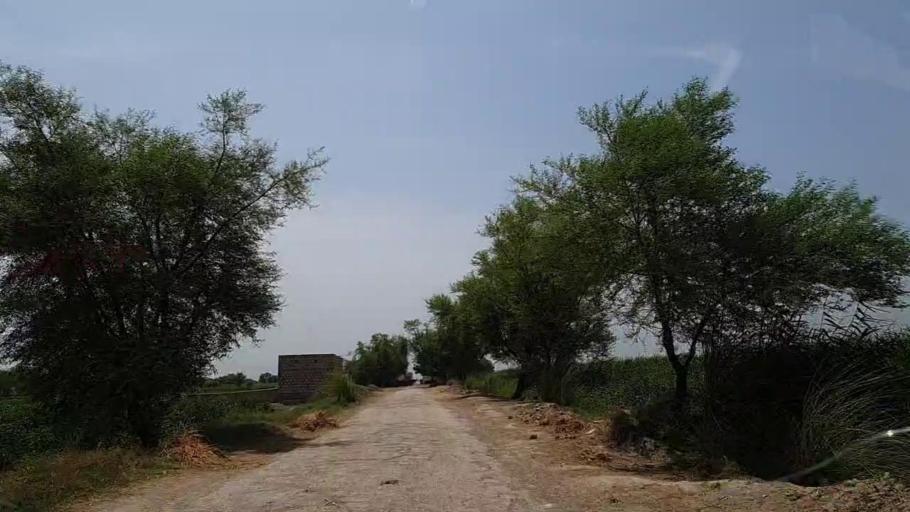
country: PK
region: Sindh
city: Khanpur
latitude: 27.8840
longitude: 69.4933
